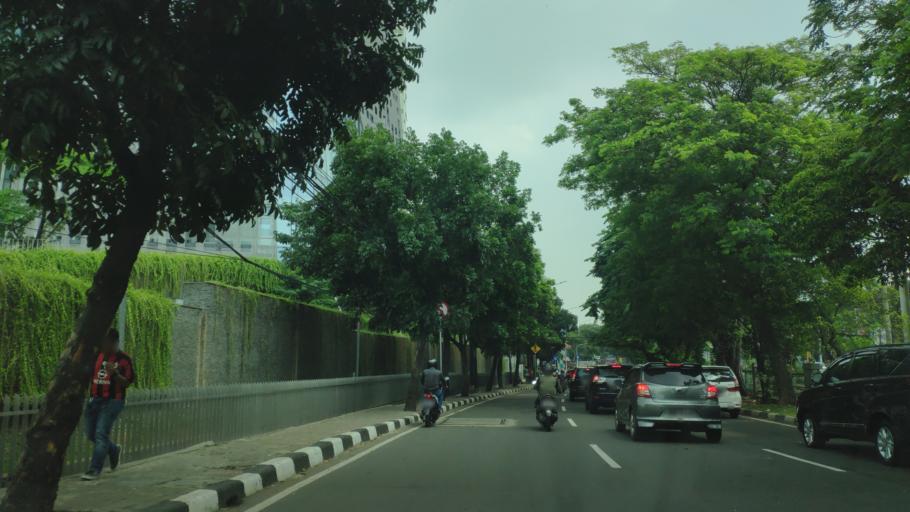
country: ID
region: Jakarta Raya
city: Jakarta
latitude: -6.2104
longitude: 106.7960
